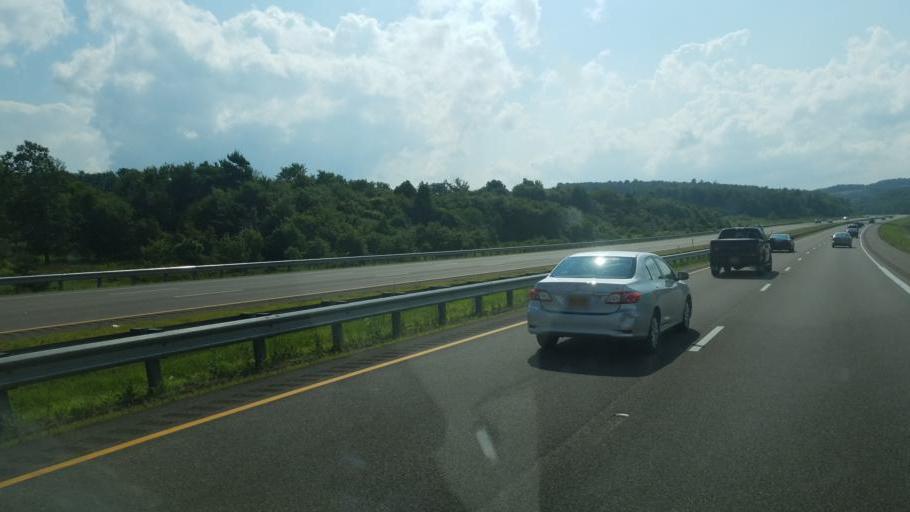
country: US
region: Maryland
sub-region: Allegany County
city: Frostburg
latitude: 39.6832
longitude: -79.0069
